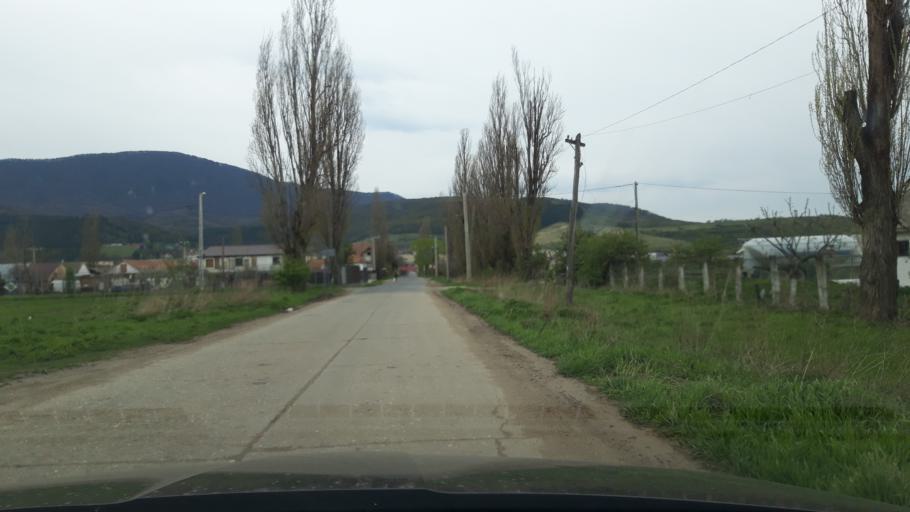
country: RO
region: Brasov
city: Codlea
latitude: 45.6991
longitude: 25.4608
